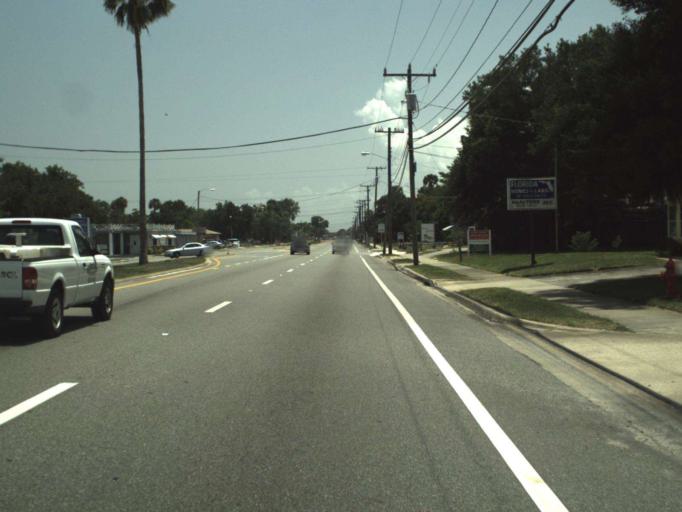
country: US
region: Florida
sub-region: Volusia County
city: Edgewater
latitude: 29.0026
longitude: -80.9133
